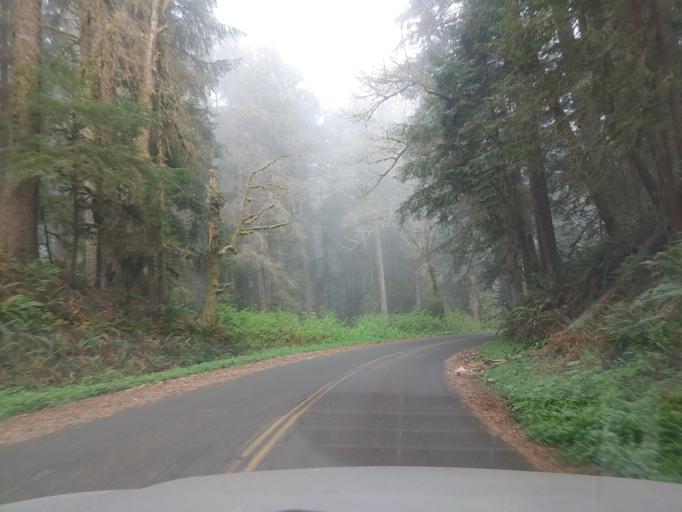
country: US
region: California
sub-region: Del Norte County
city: Bertsch-Oceanview
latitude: 41.4568
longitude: -124.0484
